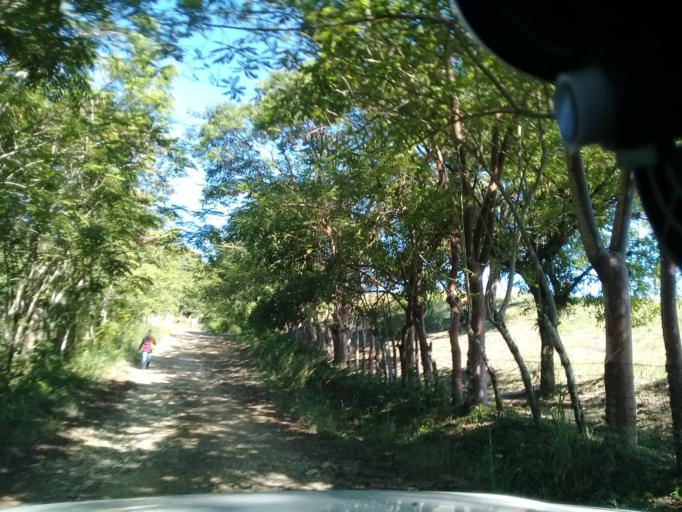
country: MX
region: Hidalgo
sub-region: Huejutla de Reyes
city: Huejutla de Reyes
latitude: 21.1634
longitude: -98.4131
